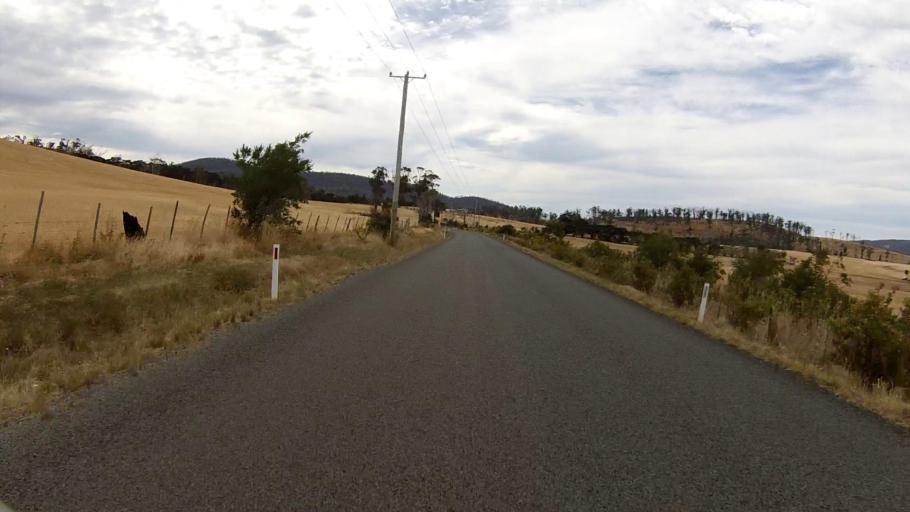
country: AU
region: Tasmania
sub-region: Sorell
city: Sorell
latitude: -42.8982
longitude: 147.7685
